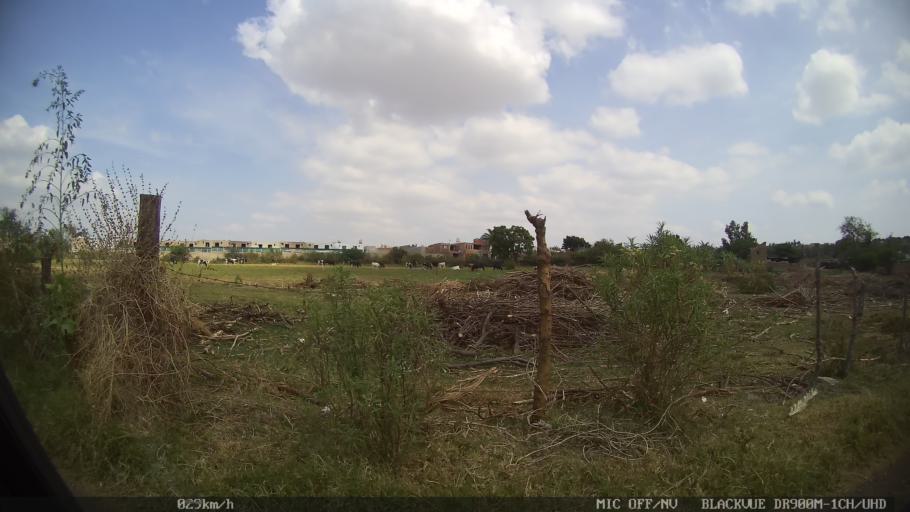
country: MX
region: Jalisco
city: Tonala
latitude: 20.6268
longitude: -103.2271
